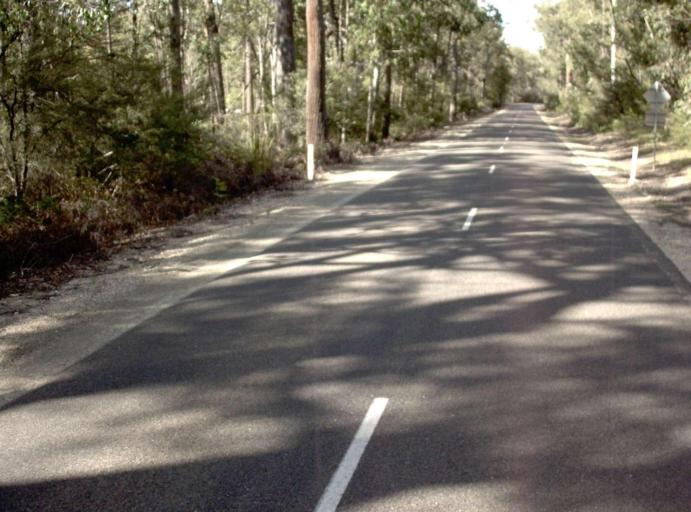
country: AU
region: Victoria
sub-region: East Gippsland
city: Lakes Entrance
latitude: -37.6621
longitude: 148.0800
